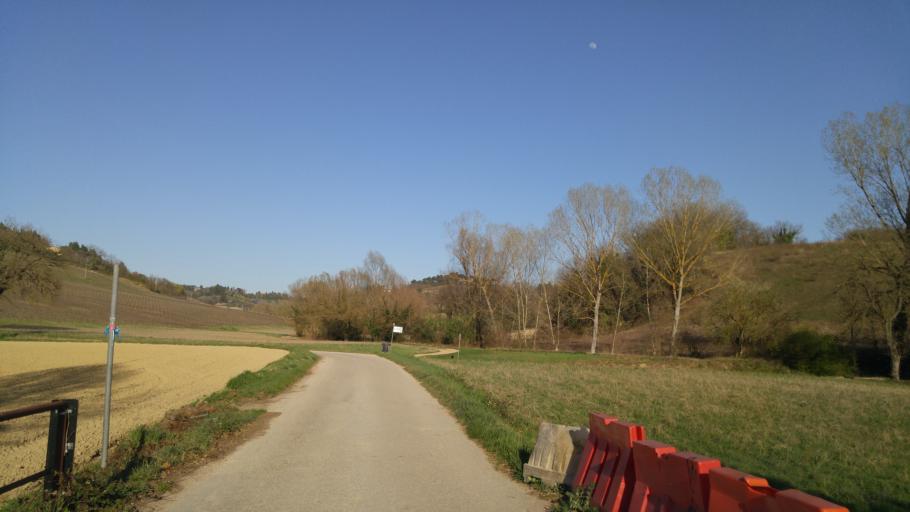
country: IT
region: The Marches
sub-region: Provincia di Pesaro e Urbino
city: Fenile
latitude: 43.8452
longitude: 12.9184
